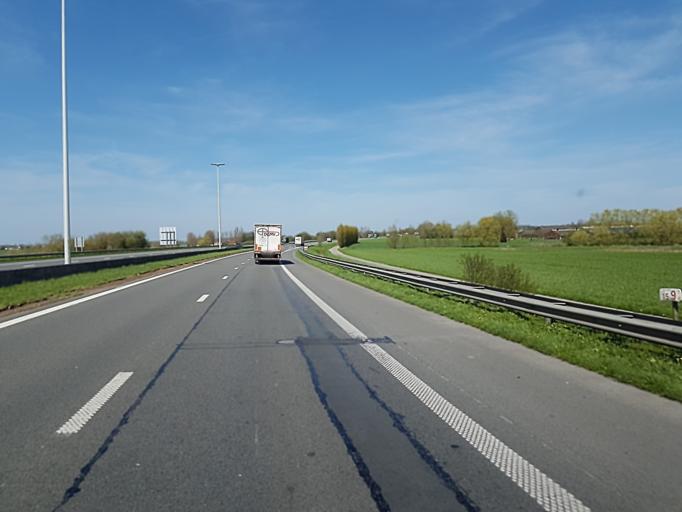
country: BE
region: Wallonia
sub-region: Province du Hainaut
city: Estaimpuis
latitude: 50.7366
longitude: 3.2915
